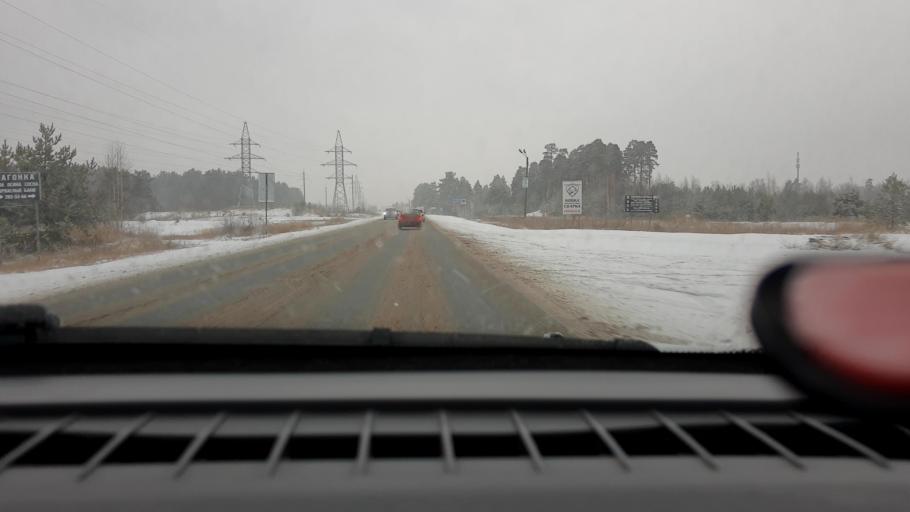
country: RU
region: Nizjnij Novgorod
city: Novaya Balakhna
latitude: 56.4679
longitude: 43.6159
